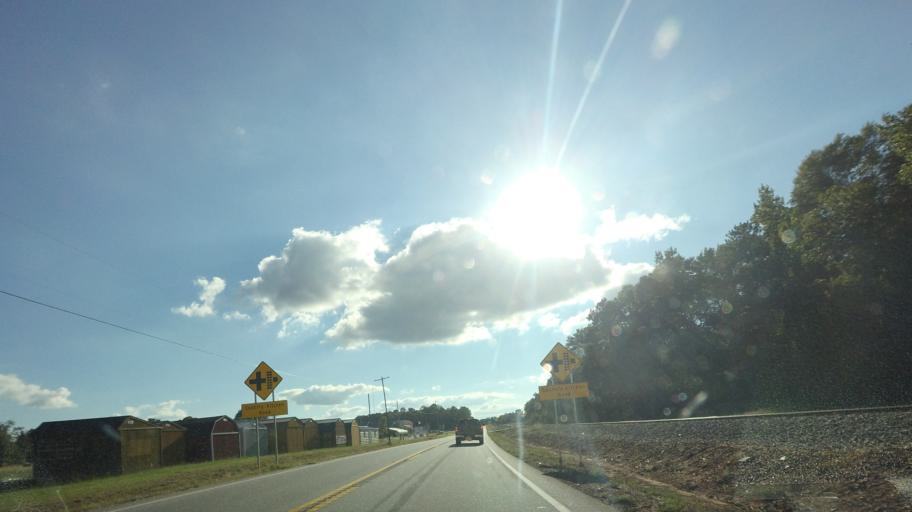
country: US
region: Georgia
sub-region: Lamar County
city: Barnesville
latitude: 33.0302
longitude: -84.1694
